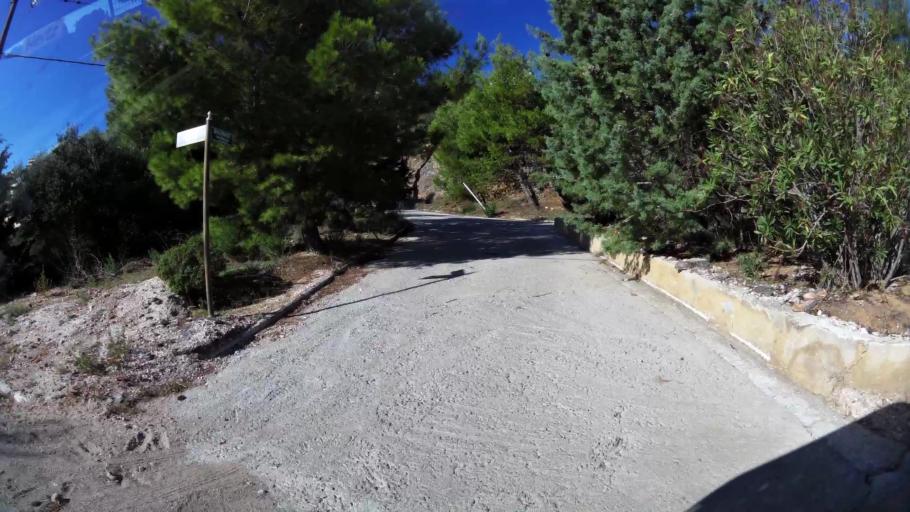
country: GR
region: Attica
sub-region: Nomarchia Anatolikis Attikis
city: Dhrafi
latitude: 38.0344
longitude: 23.8944
